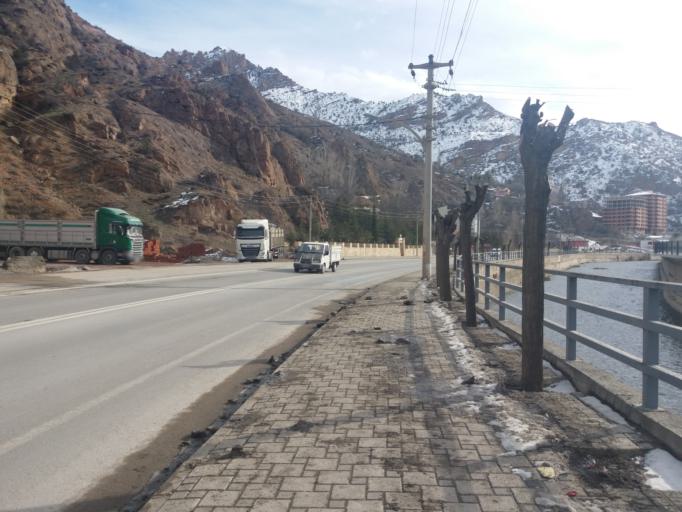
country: TR
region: Gumushane
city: Gumushkhane
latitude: 40.4473
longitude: 39.5008
